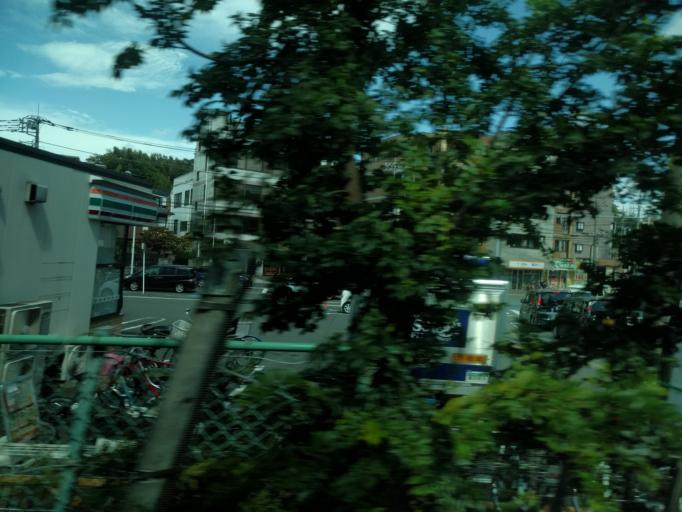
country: JP
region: Tokyo
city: Chofugaoka
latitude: 35.6022
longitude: 139.6036
